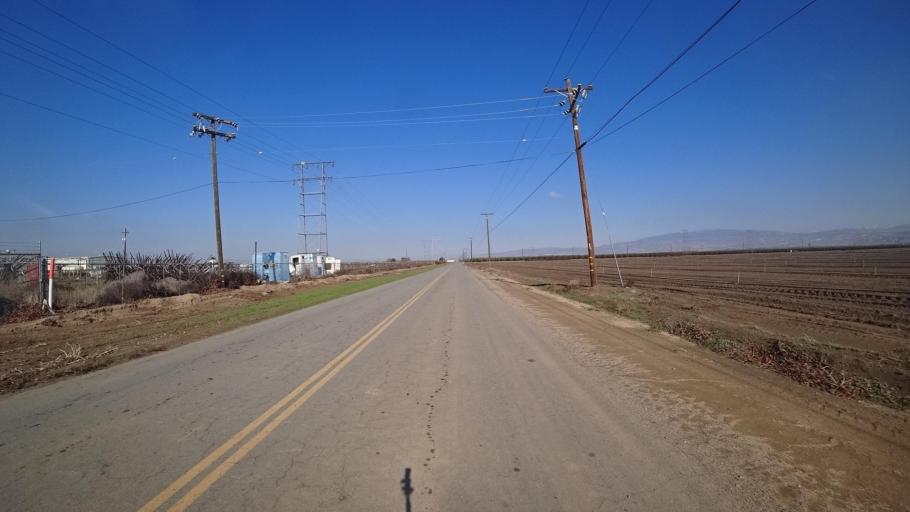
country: US
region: California
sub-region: Kern County
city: Arvin
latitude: 35.2202
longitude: -118.8064
